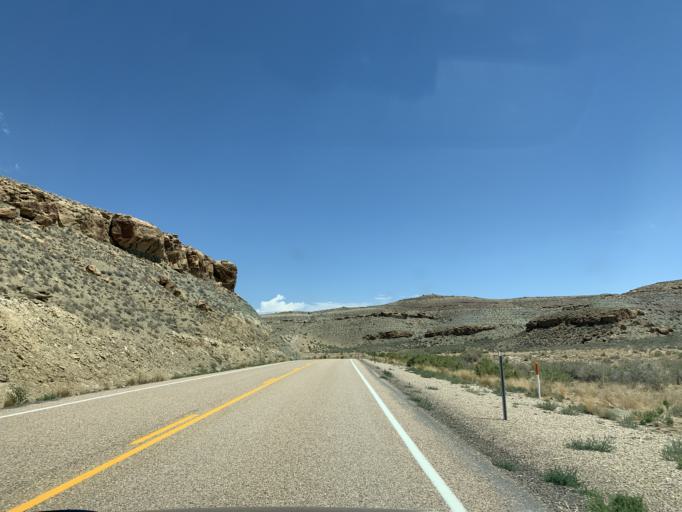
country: US
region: Utah
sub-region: Duchesne County
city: Duchesne
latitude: 40.0101
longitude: -110.1521
